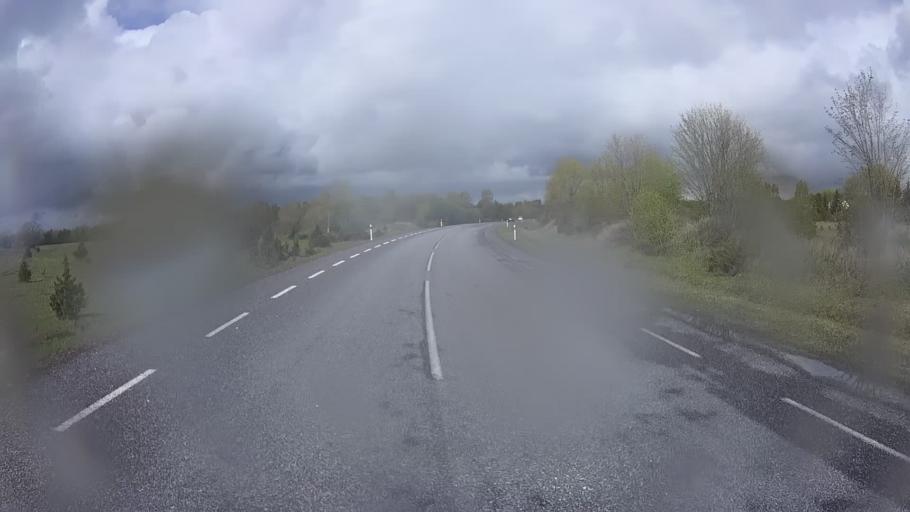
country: EE
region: Hiiumaa
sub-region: Kaerdla linn
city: Kardla
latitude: 58.8763
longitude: 22.9515
